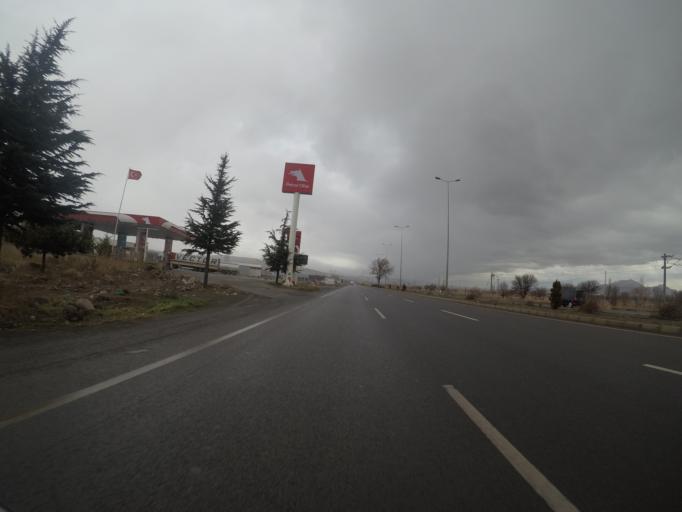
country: TR
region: Kayseri
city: Incesu
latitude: 38.7000
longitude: 35.2519
